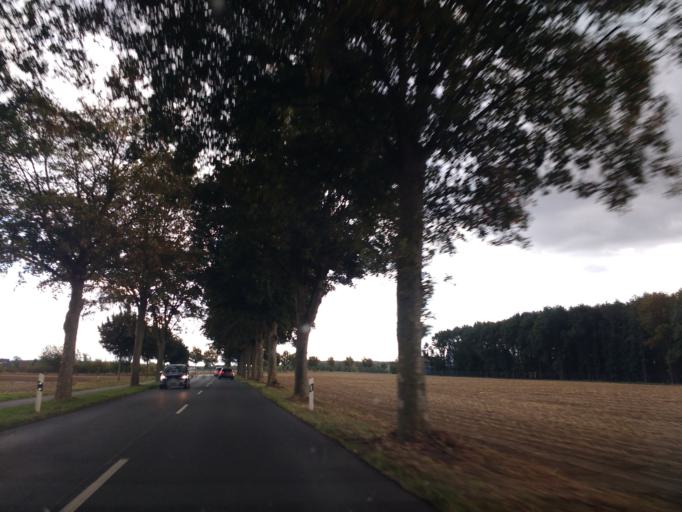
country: DE
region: North Rhine-Westphalia
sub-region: Regierungsbezirk Dusseldorf
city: Xanten
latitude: 51.6771
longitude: 6.4433
